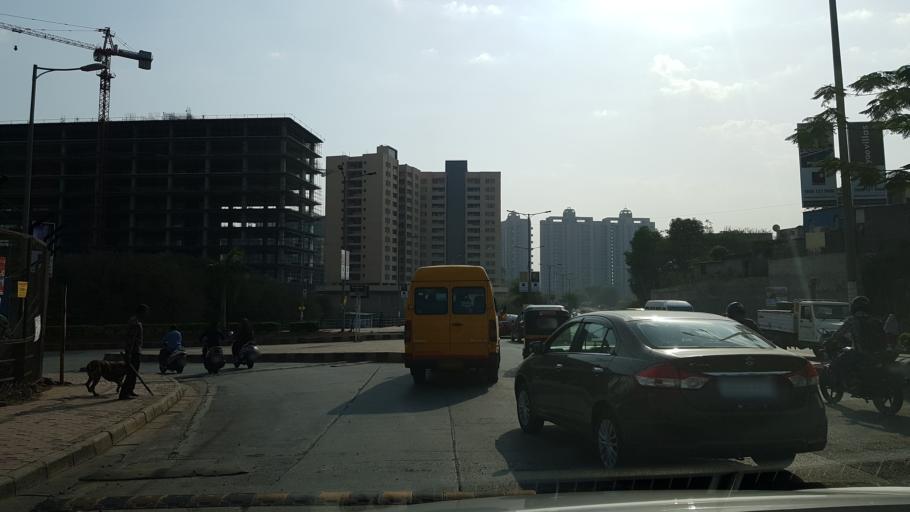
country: IN
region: Maharashtra
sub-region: Pune Division
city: Lohogaon
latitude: 18.5485
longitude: 73.9468
